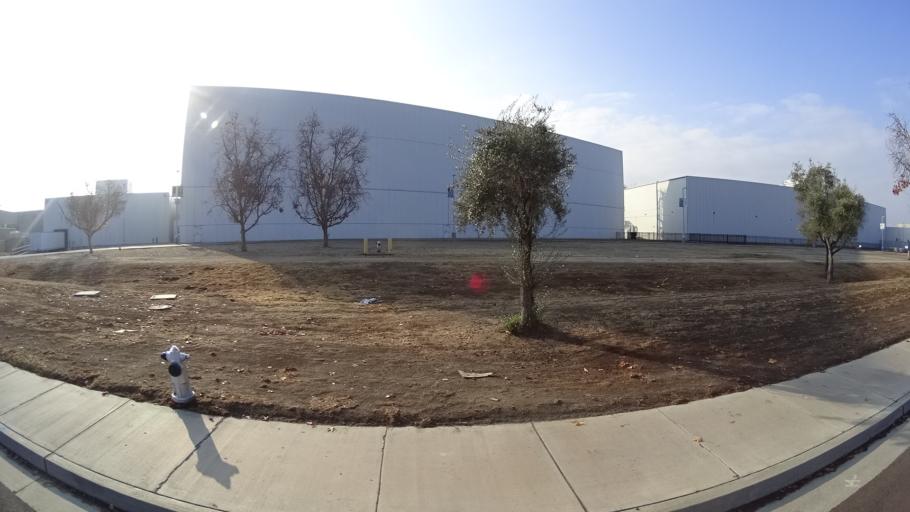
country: US
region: California
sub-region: Kern County
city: Greenacres
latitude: 35.3131
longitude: -119.0860
